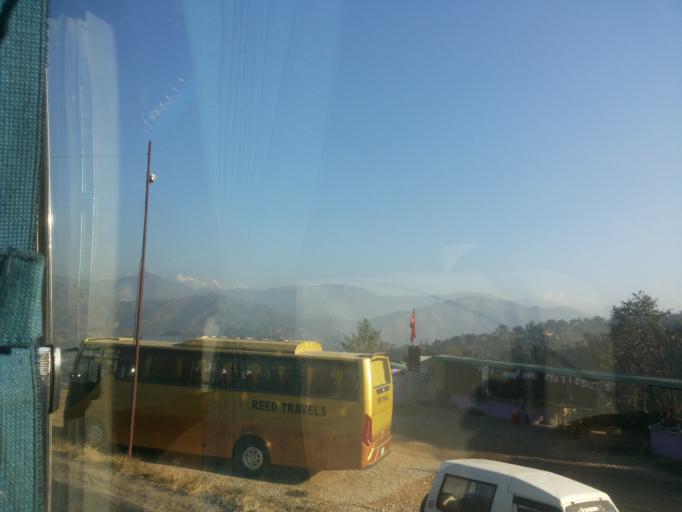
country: NP
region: Central Region
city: Kirtipur
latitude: 27.7136
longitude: 85.1803
